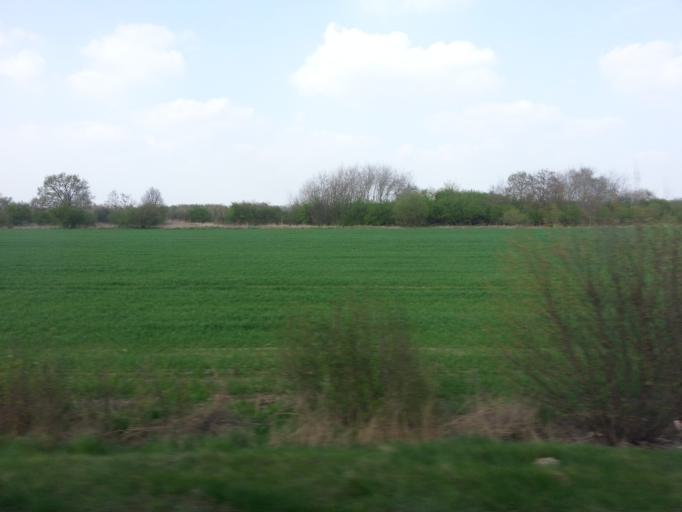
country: DE
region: Brandenburg
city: Velten
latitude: 52.7057
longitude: 13.1573
